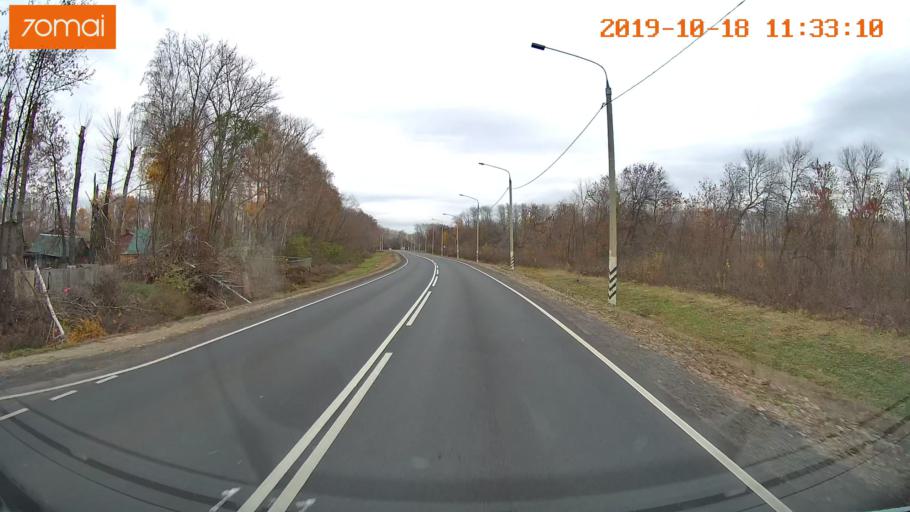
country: RU
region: Rjazan
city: Oktyabr'skiy
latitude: 54.1418
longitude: 38.7339
